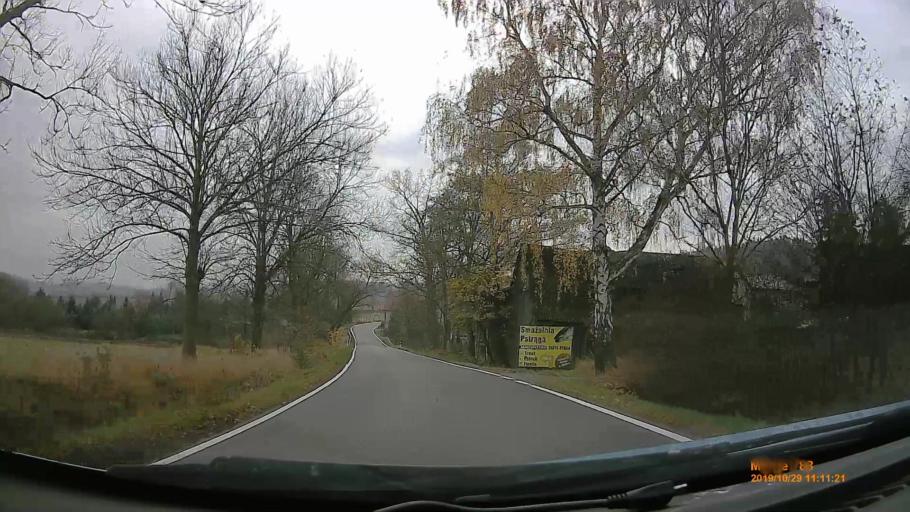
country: PL
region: Lower Silesian Voivodeship
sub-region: Powiat klodzki
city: Polanica-Zdroj
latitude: 50.4357
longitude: 16.5030
